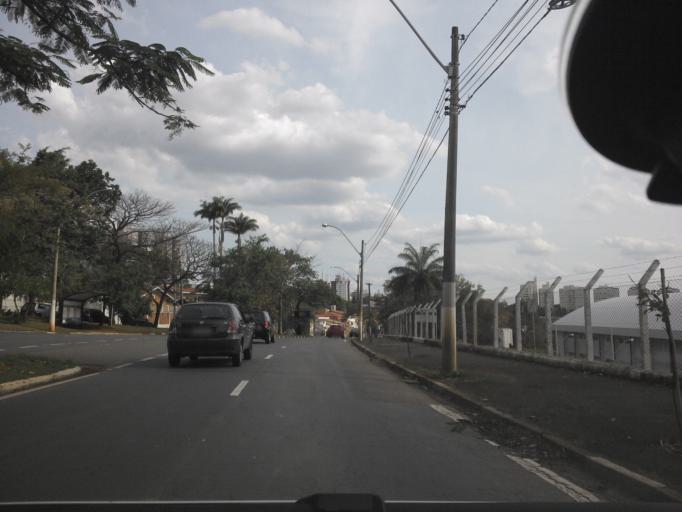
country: BR
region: Sao Paulo
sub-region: Campinas
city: Campinas
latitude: -22.8807
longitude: -47.0754
